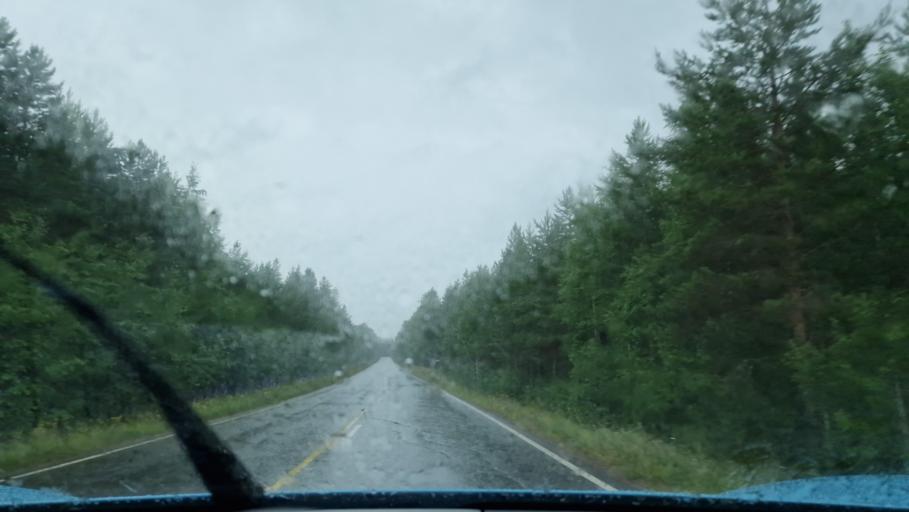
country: FI
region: Southern Ostrobothnia
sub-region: Jaerviseutu
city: Soini
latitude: 62.8311
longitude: 24.3379
